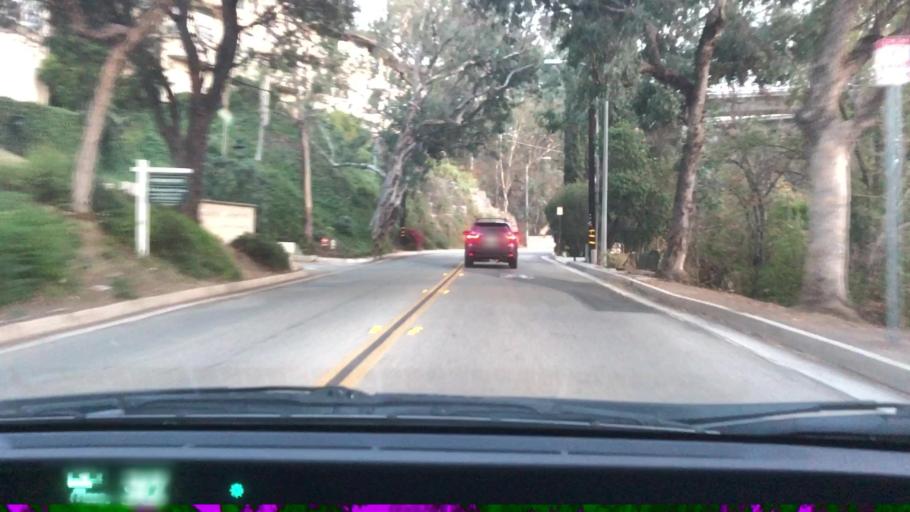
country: US
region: California
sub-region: Los Angeles County
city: Pasadena
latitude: 34.1473
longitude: -118.1646
